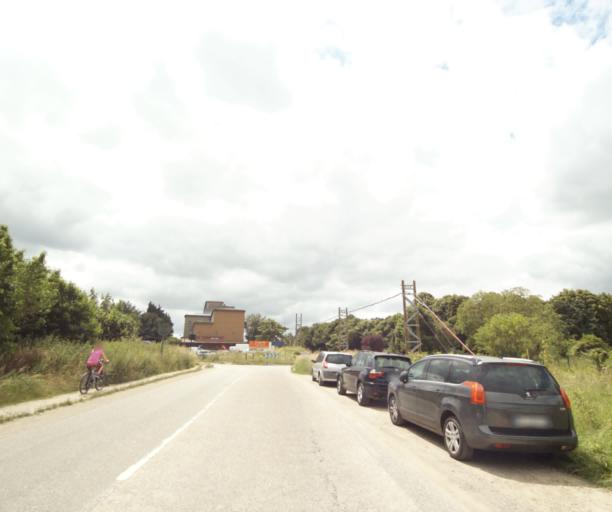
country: FR
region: Ile-de-France
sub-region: Departement des Yvelines
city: Saint-Cyr-l'Ecole
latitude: 48.8159
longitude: 2.0792
